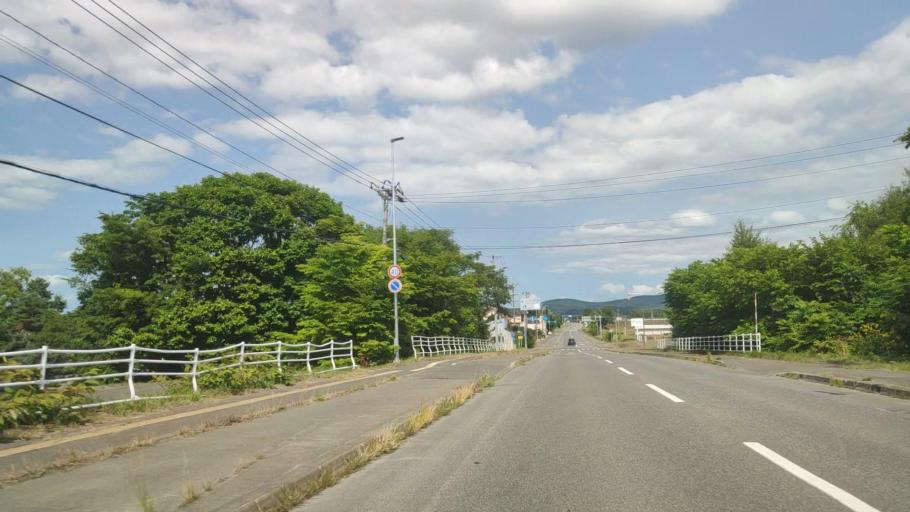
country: JP
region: Hokkaido
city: Nayoro
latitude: 44.1873
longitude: 142.4071
